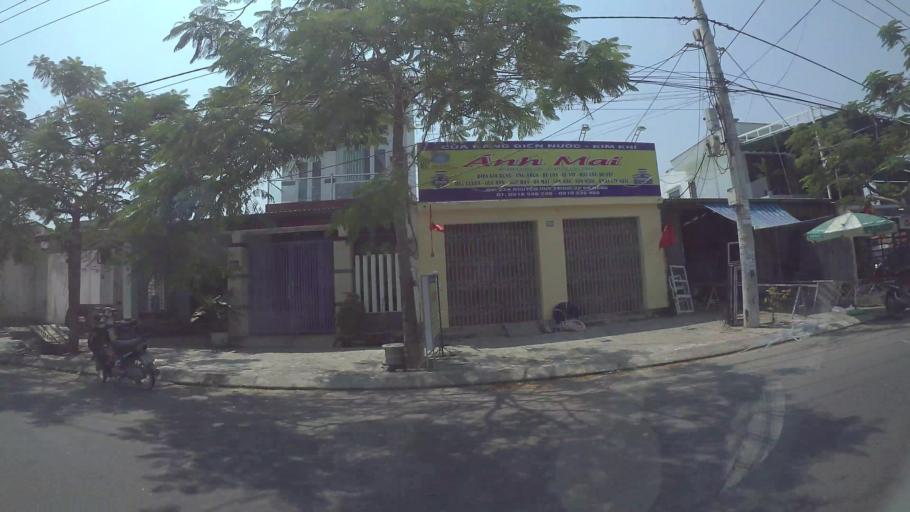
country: VN
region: Da Nang
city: Ngu Hanh Son
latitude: 15.9924
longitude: 108.2663
